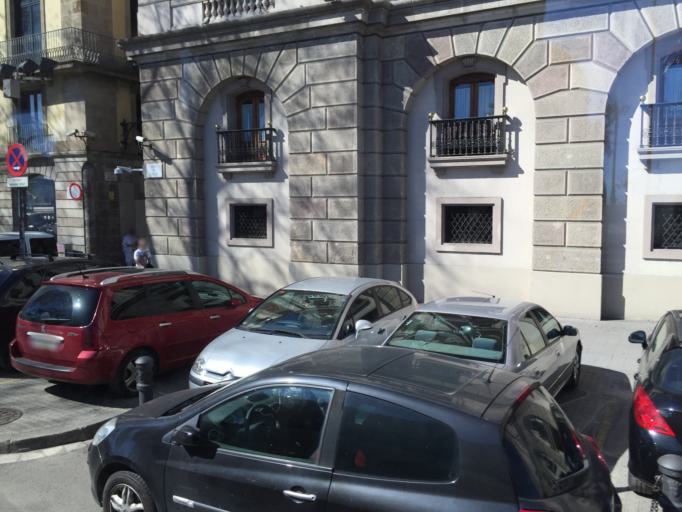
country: ES
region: Catalonia
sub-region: Provincia de Barcelona
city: Ciutat Vella
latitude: 41.3793
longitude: 2.1804
